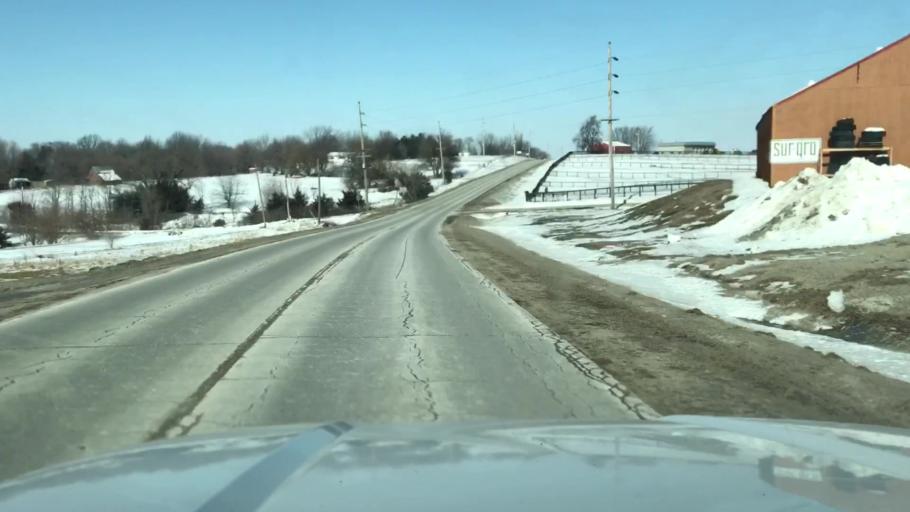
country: US
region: Missouri
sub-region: Andrew County
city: Savannah
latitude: 39.9512
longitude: -94.8461
